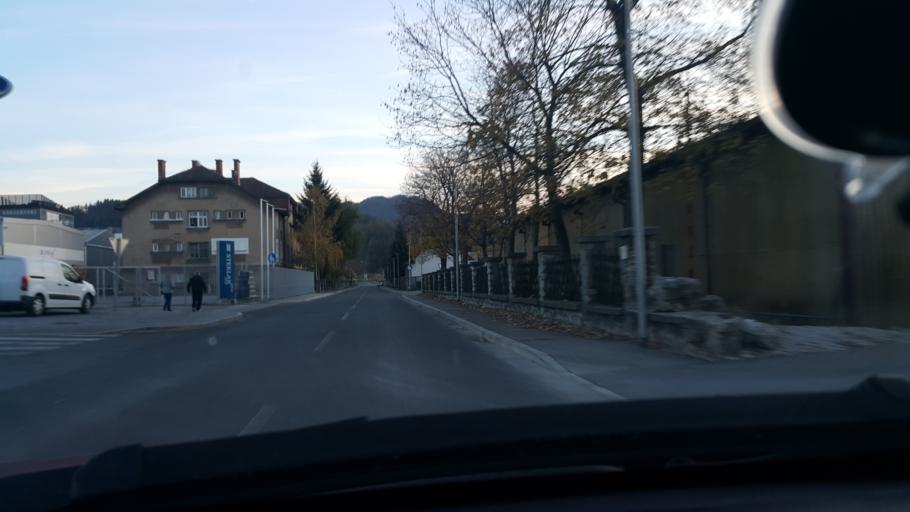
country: SI
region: Celje
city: Celje
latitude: 46.2379
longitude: 15.2763
